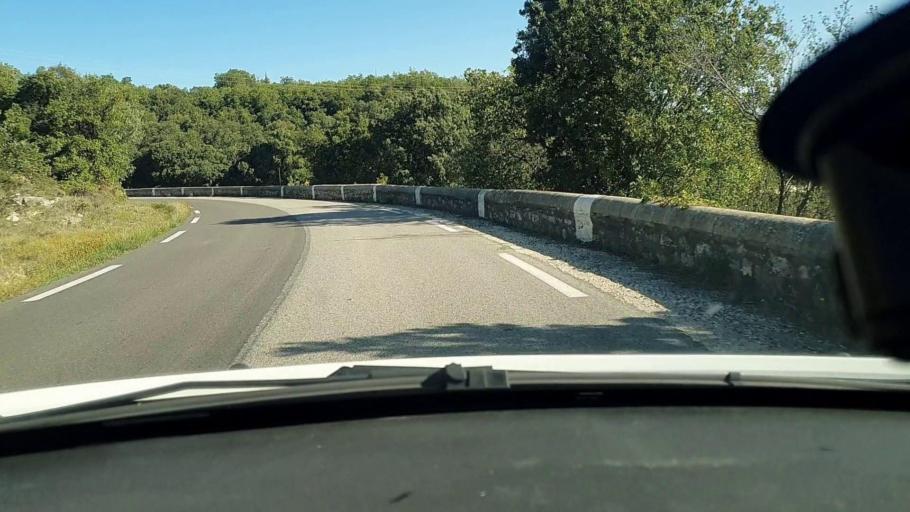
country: FR
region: Languedoc-Roussillon
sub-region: Departement du Gard
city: Goudargues
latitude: 44.2919
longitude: 4.4829
